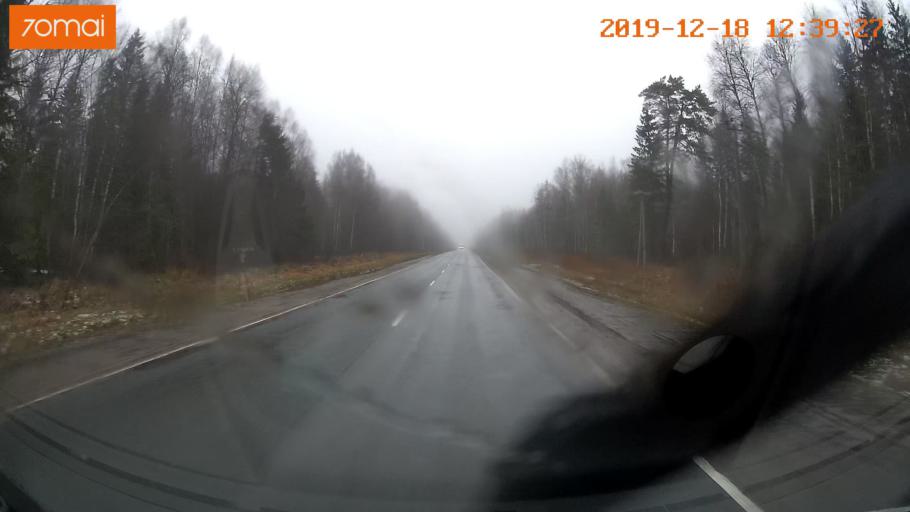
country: RU
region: Moskovskaya
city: Vysokovsk
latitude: 56.1651
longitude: 36.6115
